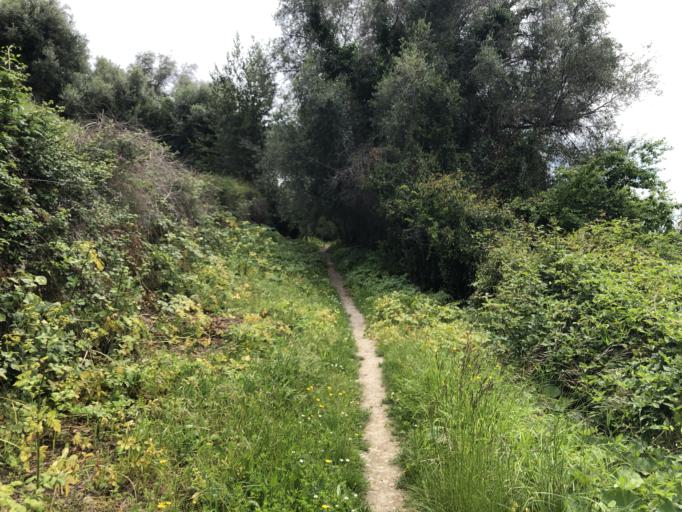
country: FR
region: Provence-Alpes-Cote d'Azur
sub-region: Departement des Alpes-Maritimes
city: Saint-Andre-de-la-Roche
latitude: 43.7234
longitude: 7.2969
